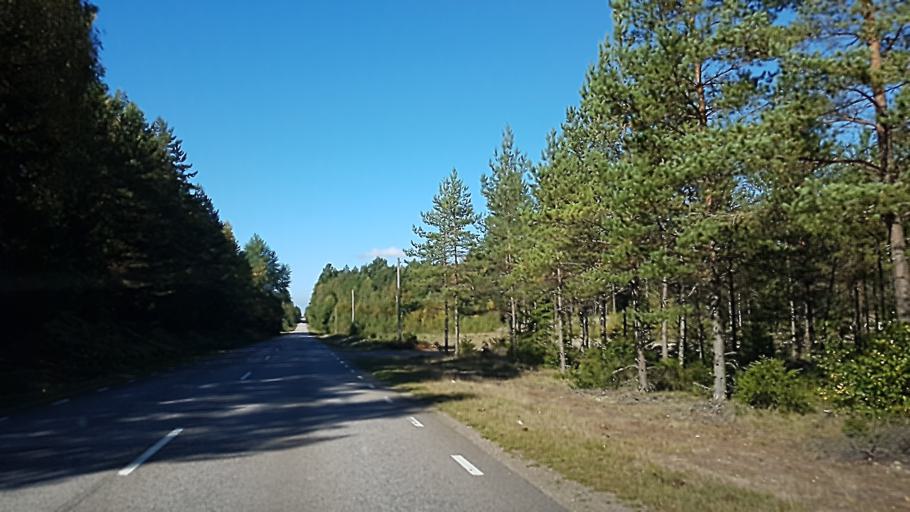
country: SE
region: Kronoberg
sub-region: Ljungby Kommun
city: Ljungby
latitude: 56.8257
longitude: 14.0508
